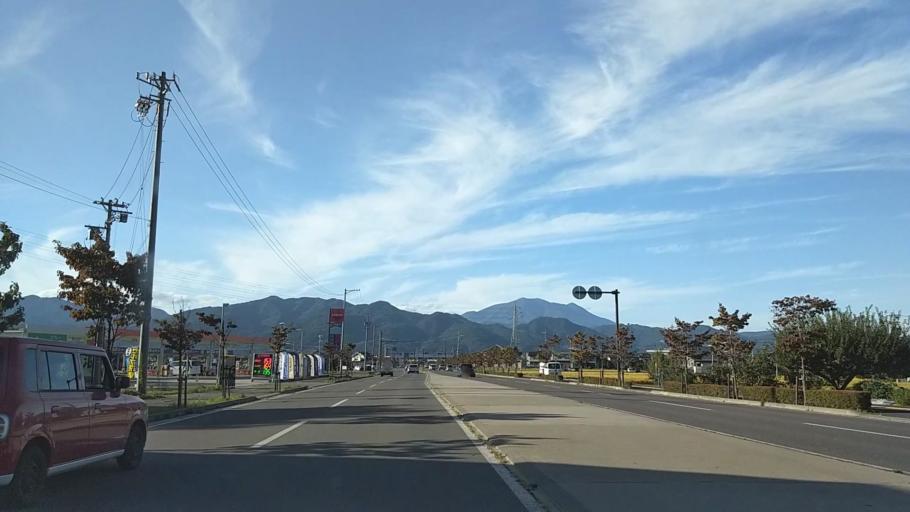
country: JP
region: Nagano
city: Nagano-shi
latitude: 36.5983
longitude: 138.1816
